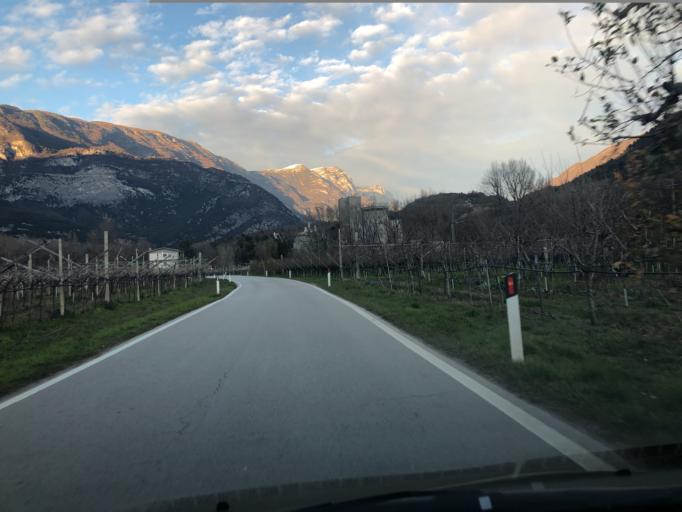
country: IT
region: Trentino-Alto Adige
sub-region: Provincia di Trento
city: Calavino
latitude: 46.0371
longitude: 10.9618
